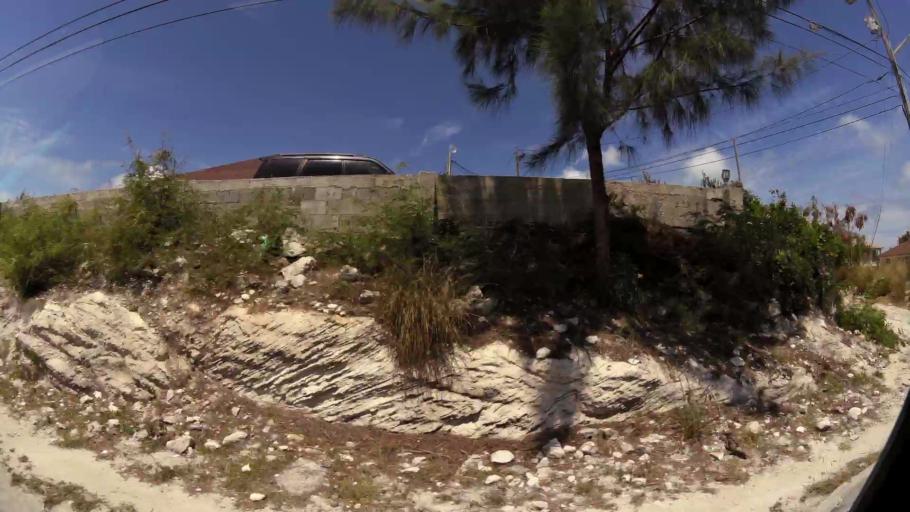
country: BS
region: Mayaguana
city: Abraham's Bay
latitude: 21.7765
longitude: -72.2651
